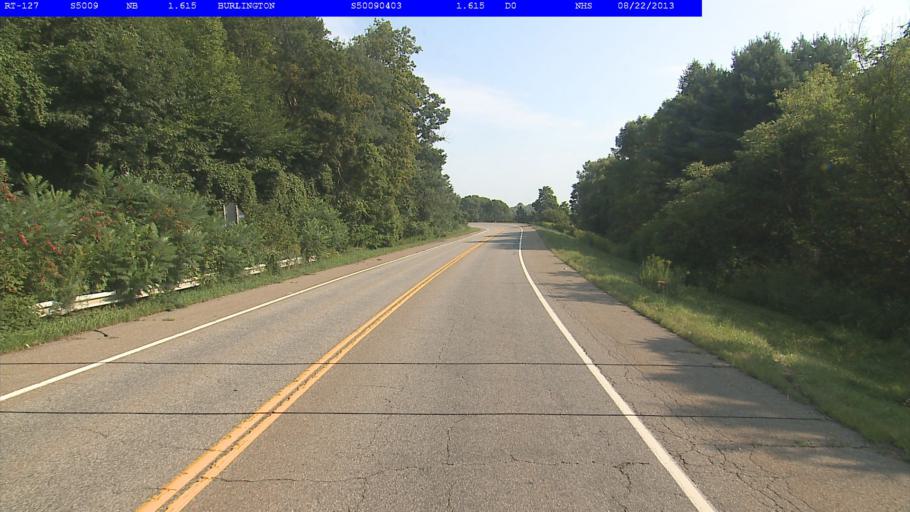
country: US
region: Vermont
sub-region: Chittenden County
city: Burlington
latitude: 44.5077
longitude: -73.2340
